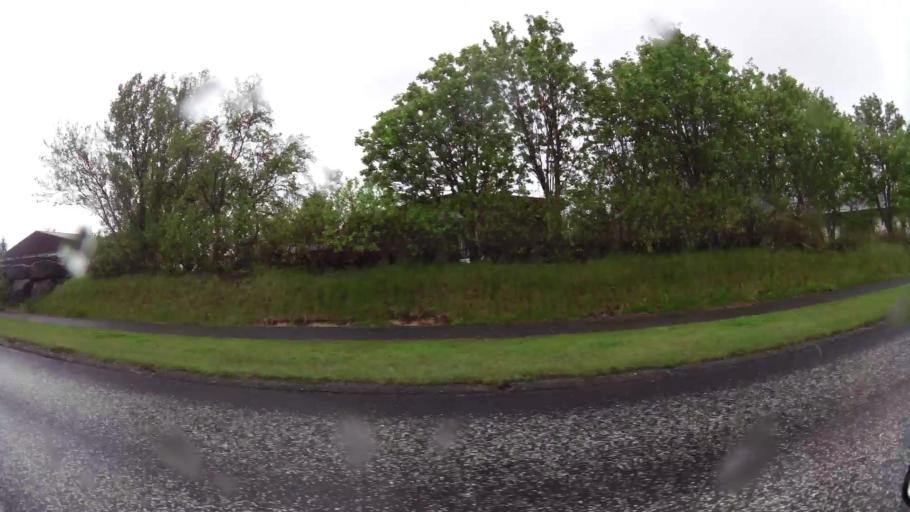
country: IS
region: Capital Region
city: Gardabaer
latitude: 64.0890
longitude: -21.9059
